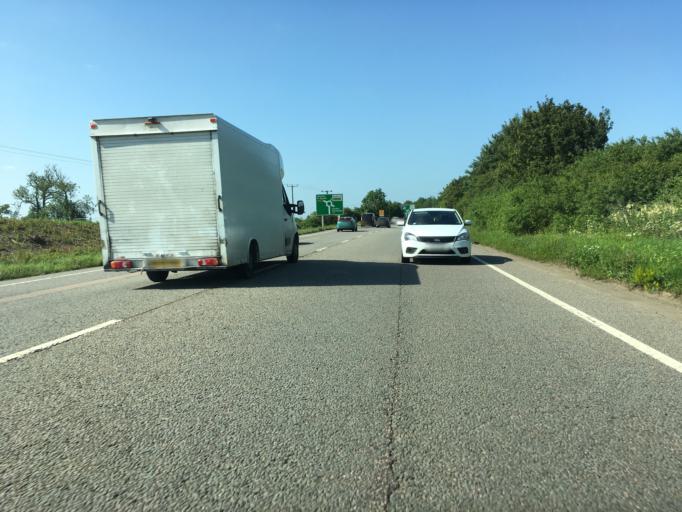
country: GB
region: England
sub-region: Milton Keynes
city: Water Eaton
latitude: 51.9889
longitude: -0.7013
